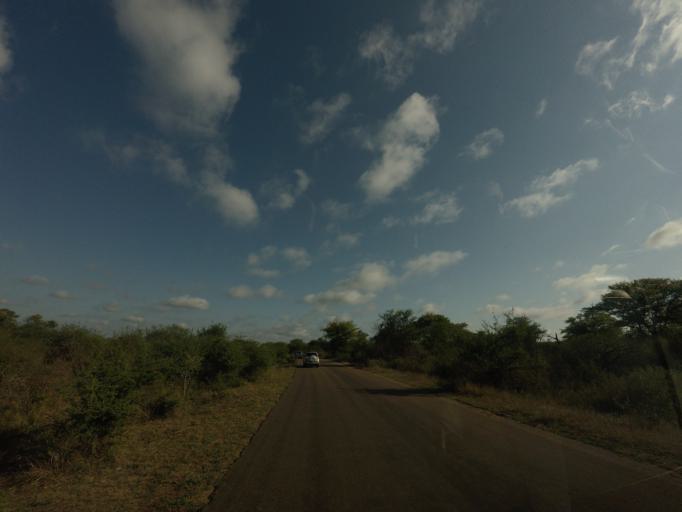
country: ZA
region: Mpumalanga
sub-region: Ehlanzeni District
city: Komatipoort
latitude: -25.2583
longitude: 31.8471
